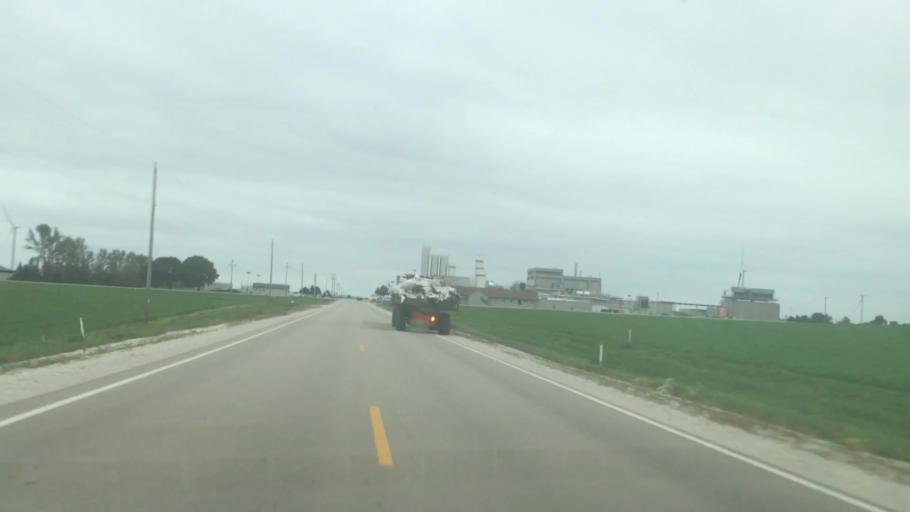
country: US
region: Wisconsin
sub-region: Fond du Lac County
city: Oakfield
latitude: 43.6197
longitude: -88.5416
